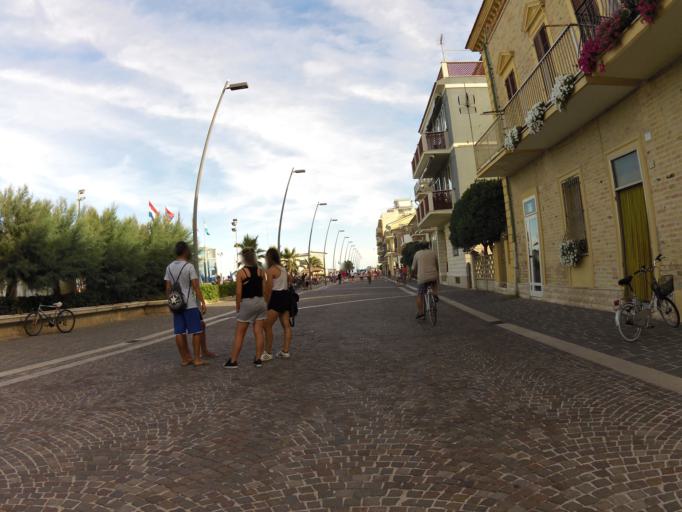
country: IT
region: The Marches
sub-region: Provincia di Macerata
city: Porto Recanati
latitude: 43.4297
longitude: 13.6672
